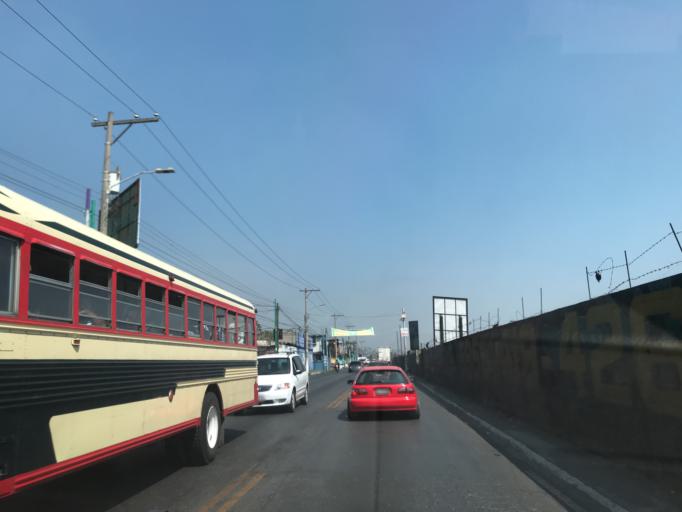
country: GT
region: Guatemala
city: Petapa
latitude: 14.5090
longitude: -90.5697
